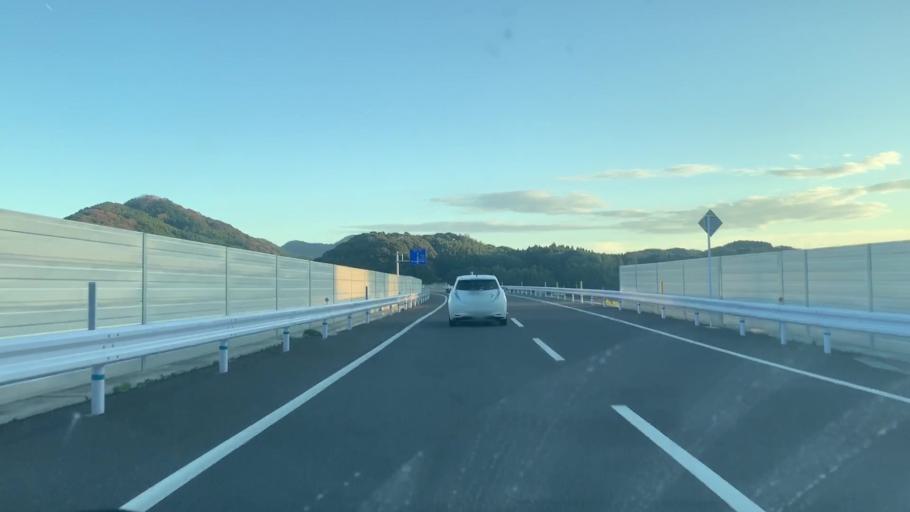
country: JP
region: Saga Prefecture
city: Takeocho-takeo
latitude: 33.2610
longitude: 129.9724
